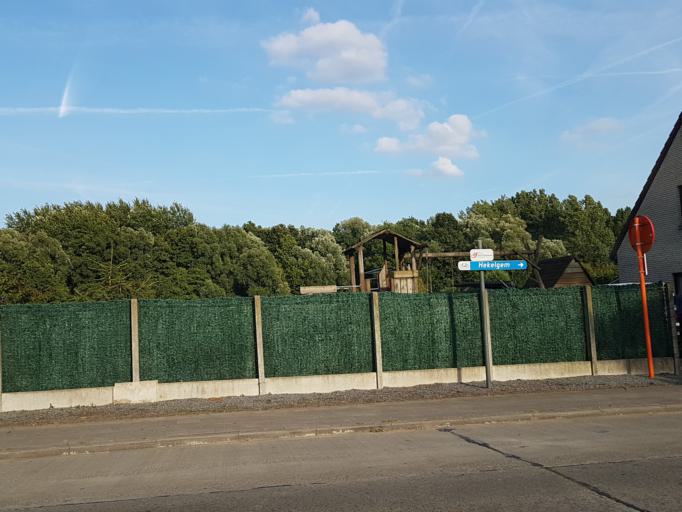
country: BE
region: Flanders
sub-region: Provincie Oost-Vlaanderen
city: Denderleeuw
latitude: 50.9438
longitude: 4.0980
